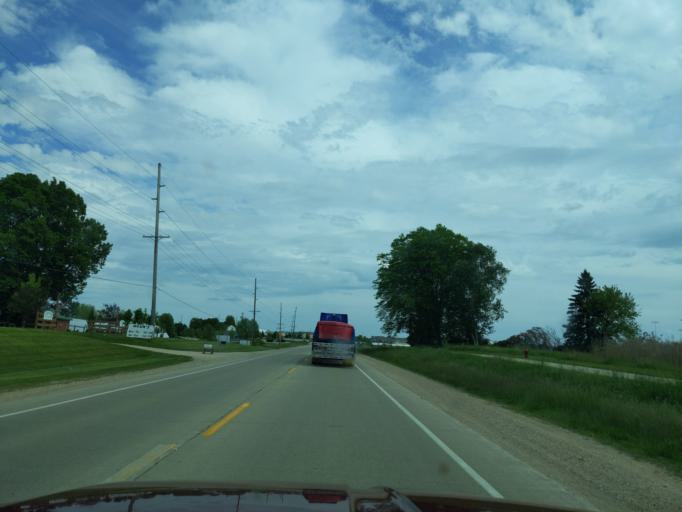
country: US
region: Wisconsin
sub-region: Dane County
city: Sun Prairie
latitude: 43.1884
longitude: -89.2739
